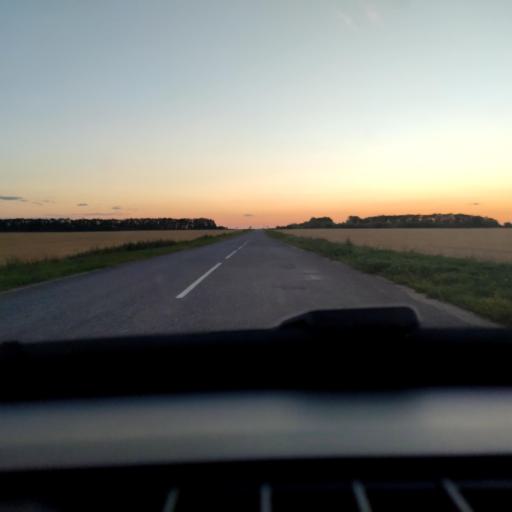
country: RU
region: Lipetsk
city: Zadonsk
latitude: 52.2978
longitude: 38.8125
